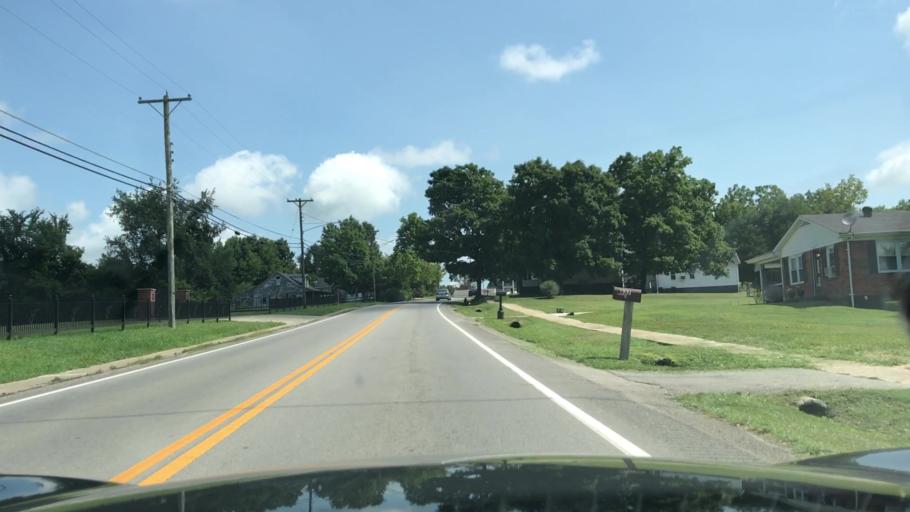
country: US
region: Kentucky
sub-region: Adair County
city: Columbia
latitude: 37.0946
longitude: -85.3162
